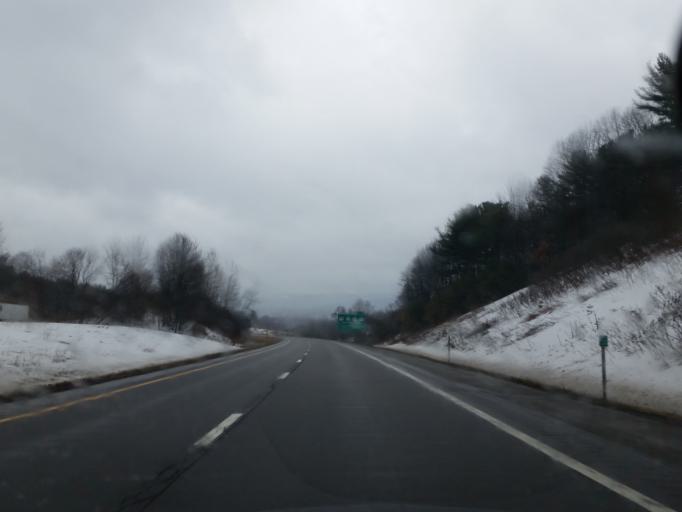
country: US
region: New York
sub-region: Chenango County
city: Lakeview
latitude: 42.3576
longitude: -75.9934
